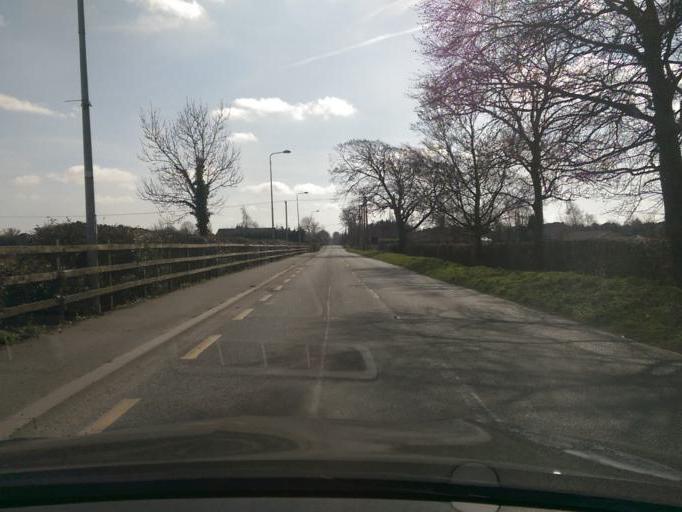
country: IE
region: Leinster
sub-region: Kildare
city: Maynooth
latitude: 53.3924
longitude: -6.5994
